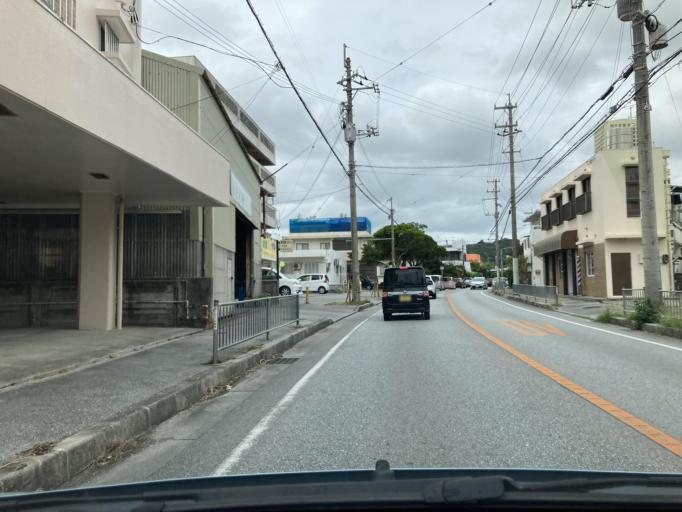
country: JP
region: Okinawa
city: Ginowan
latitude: 26.2260
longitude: 127.7572
